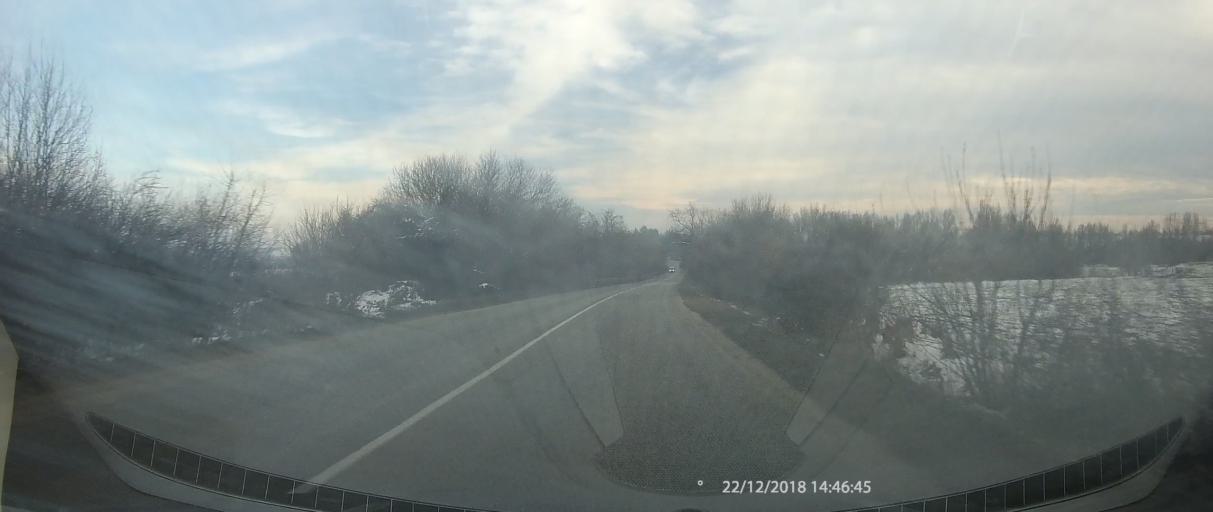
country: BG
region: Veliko Turnovo
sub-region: Obshtina Pavlikeni
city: Pavlikeni
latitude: 43.4156
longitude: 25.3690
